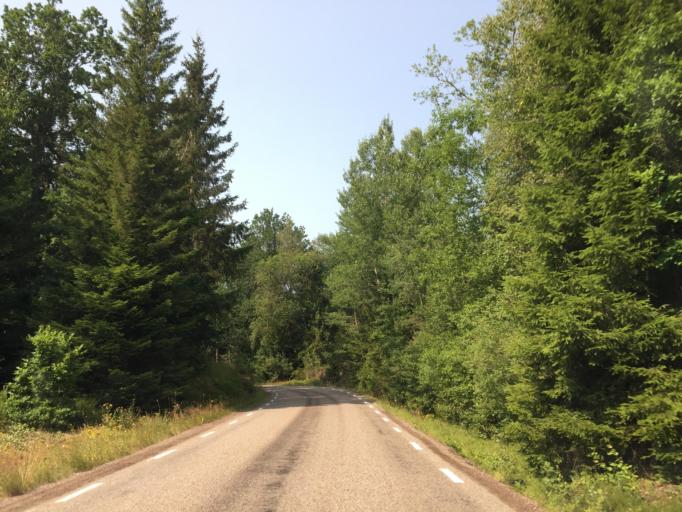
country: SE
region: Vaestra Goetaland
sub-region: Trollhattan
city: Sjuntorp
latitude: 58.3082
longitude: 12.1280
